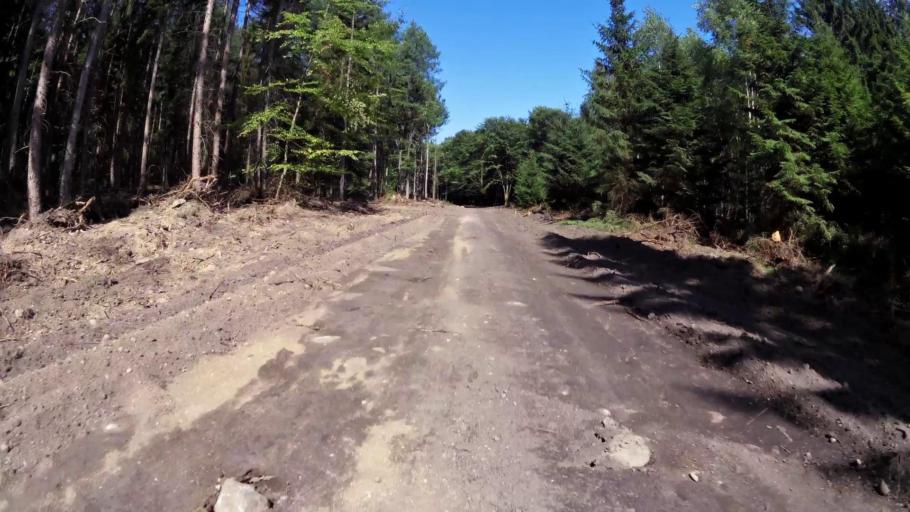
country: PL
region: West Pomeranian Voivodeship
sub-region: Powiat drawski
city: Wierzchowo
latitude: 53.4118
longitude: 16.2326
